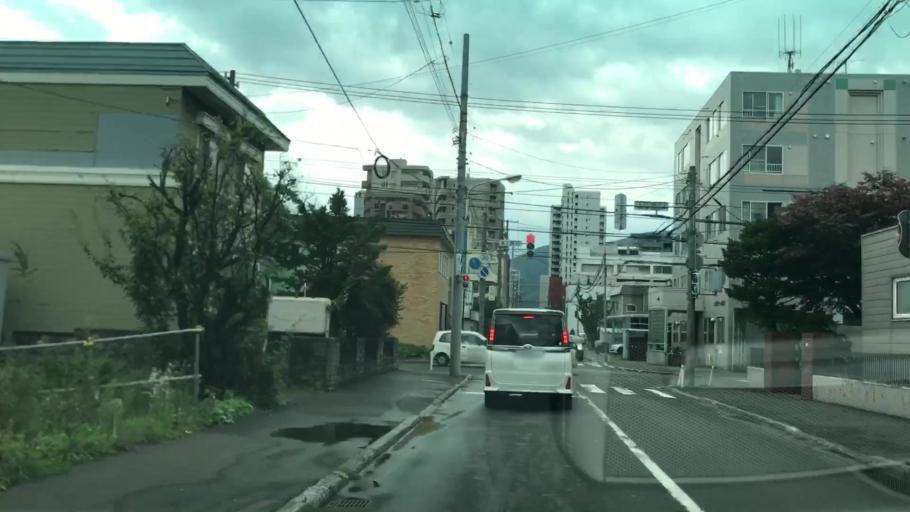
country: JP
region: Hokkaido
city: Sapporo
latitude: 43.0606
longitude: 141.3208
